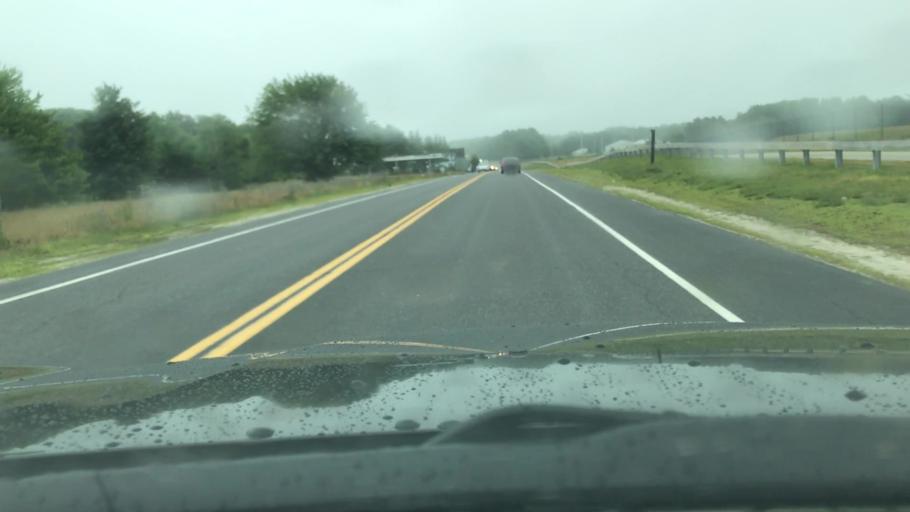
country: US
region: Maine
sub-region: Cumberland County
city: Brunswick
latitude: 43.9074
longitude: -69.9383
